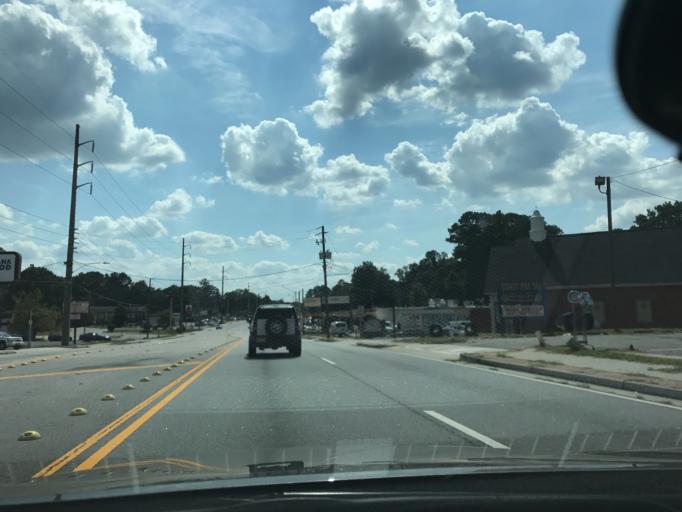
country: US
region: Georgia
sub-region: DeKalb County
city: Belvedere Park
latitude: 33.7517
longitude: -84.2729
